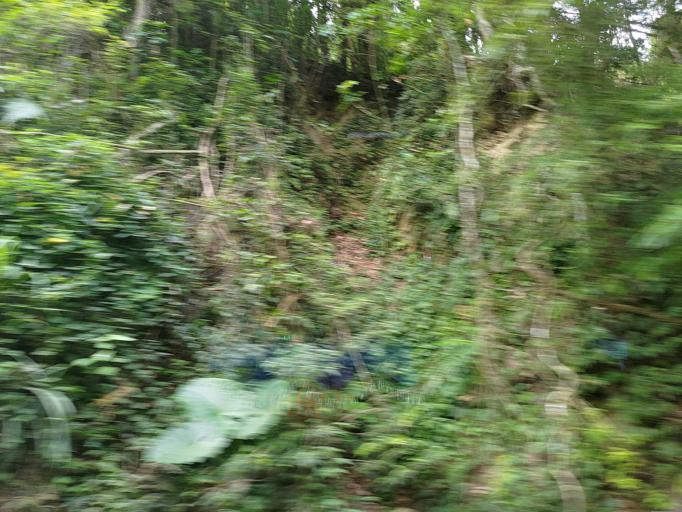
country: TW
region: Taiwan
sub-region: Hsinchu
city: Hsinchu
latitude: 24.6213
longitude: 121.0425
